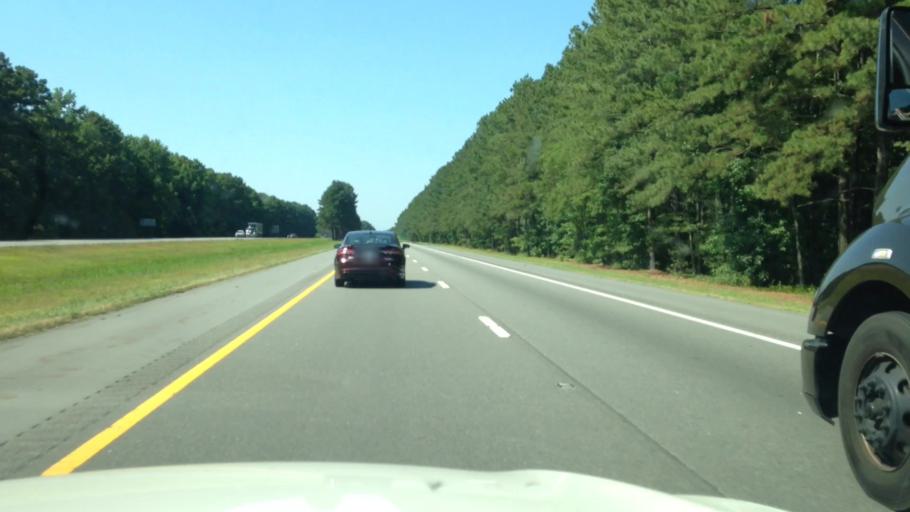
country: US
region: North Carolina
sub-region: Nash County
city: Red Oak
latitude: 36.0910
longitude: -77.8070
